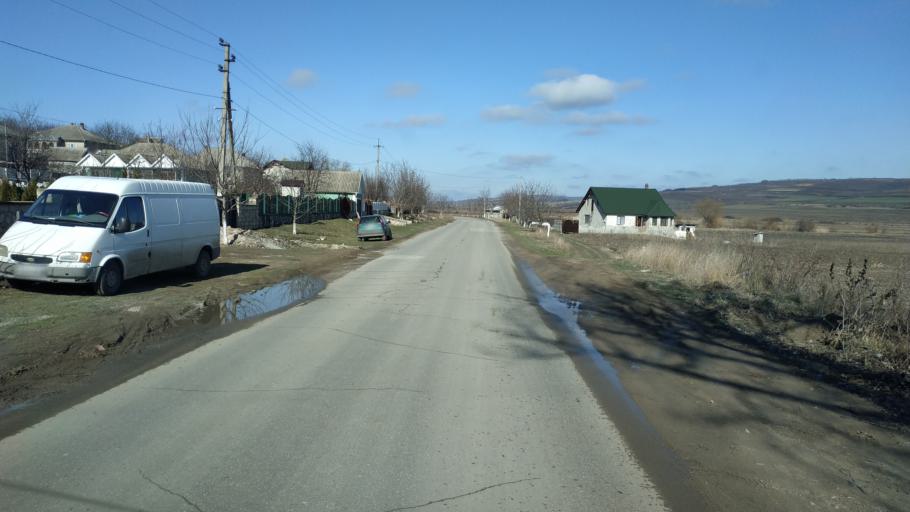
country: MD
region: Hincesti
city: Hincesti
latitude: 46.9363
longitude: 28.6379
